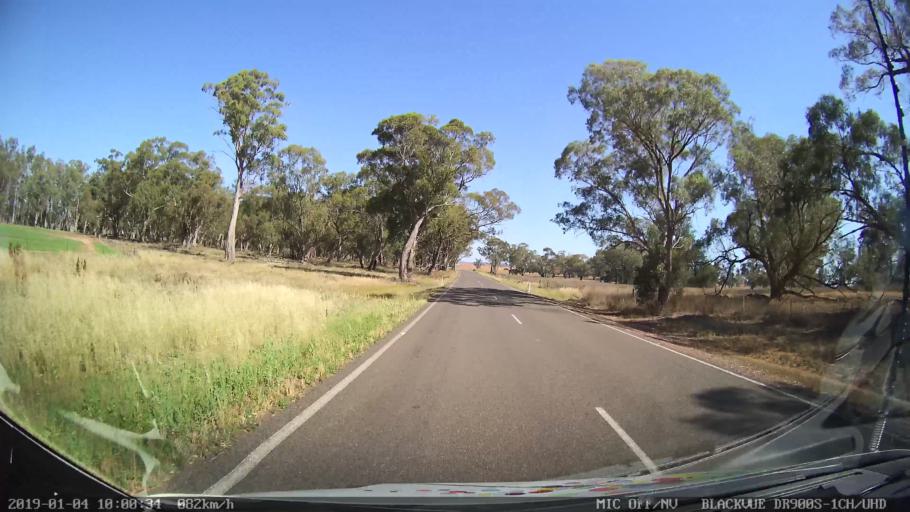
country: AU
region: New South Wales
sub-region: Cabonne
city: Canowindra
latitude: -33.4962
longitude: 148.3781
